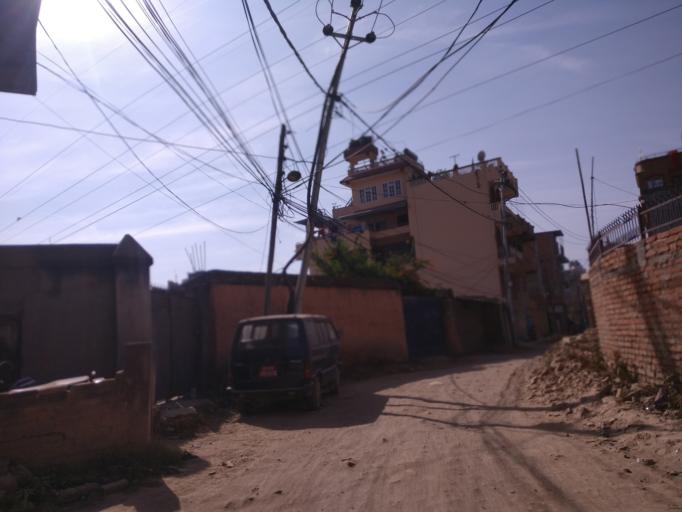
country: NP
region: Central Region
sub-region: Bagmati Zone
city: Patan
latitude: 27.6705
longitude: 85.3366
